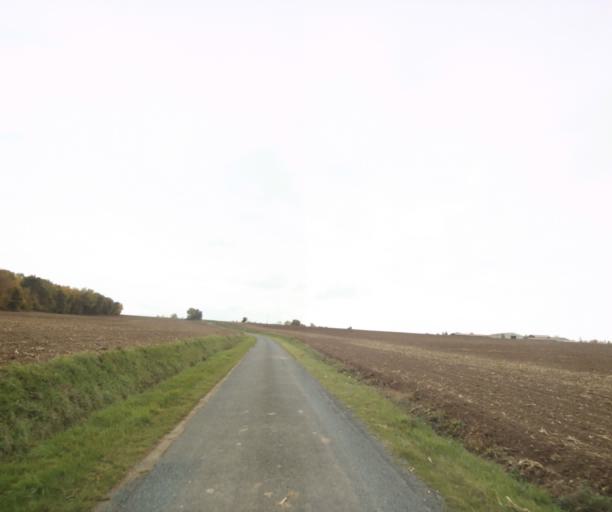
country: FR
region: Poitou-Charentes
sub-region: Departement de la Charente-Maritime
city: Saint-Georges-des-Coteaux
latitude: 45.7750
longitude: -0.7118
